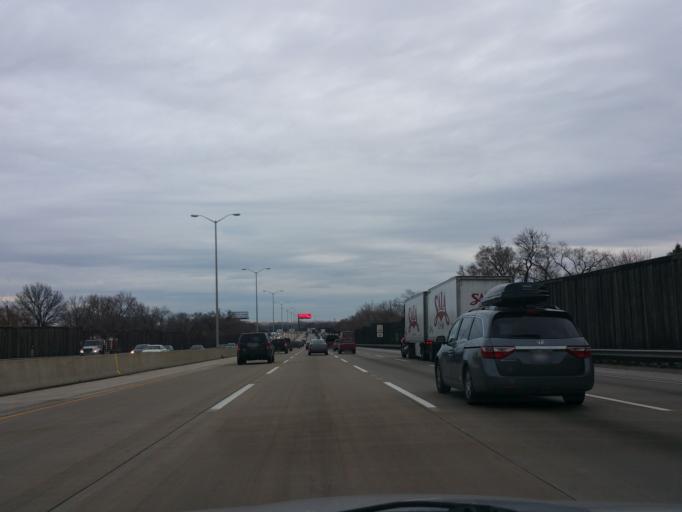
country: US
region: Illinois
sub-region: Cook County
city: Chicago Ridge
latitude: 41.6892
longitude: -87.7829
